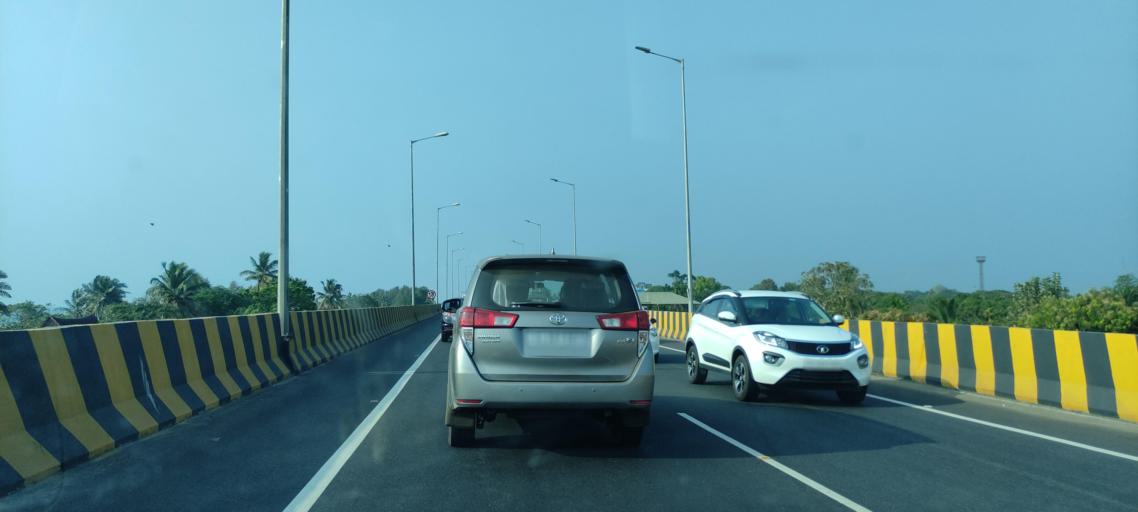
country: IN
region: Kerala
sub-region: Alappuzha
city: Alleppey
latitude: 9.4832
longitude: 76.3210
